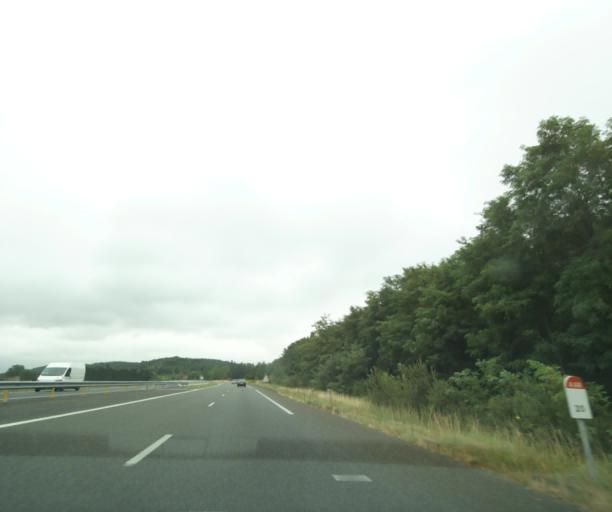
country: FR
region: Midi-Pyrenees
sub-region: Departement de la Haute-Garonne
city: Buzet-sur-Tarn
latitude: 43.7472
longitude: 1.6261
